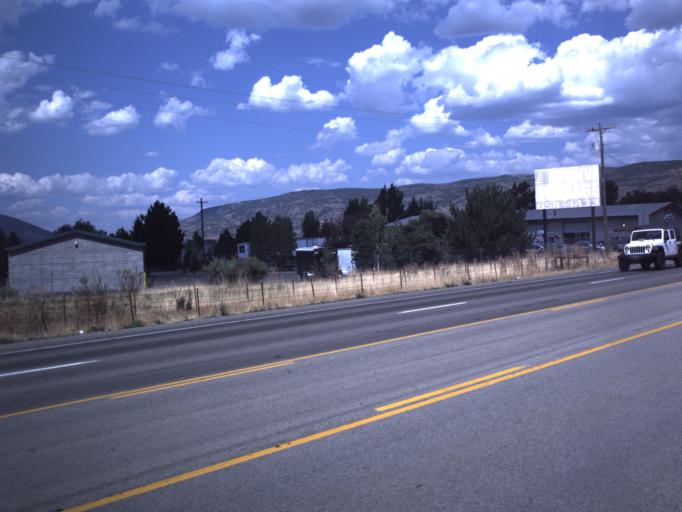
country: US
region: Utah
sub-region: Wasatch County
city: Heber
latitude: 40.4885
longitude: -111.4202
